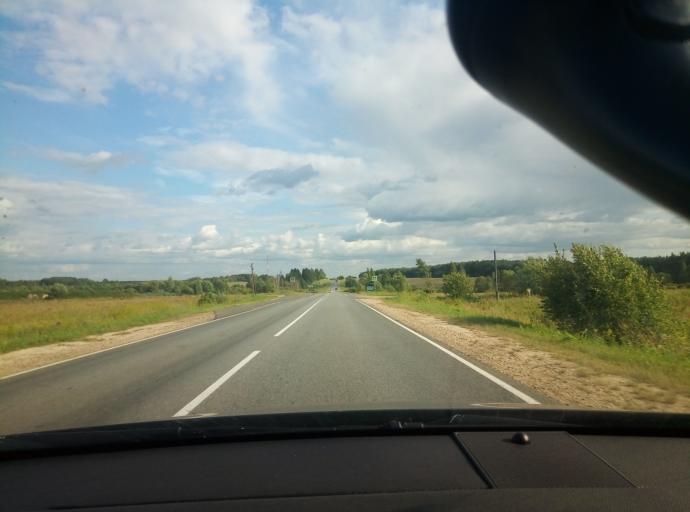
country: RU
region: Kaluga
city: Yukhnov
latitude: 54.6190
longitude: 35.3507
